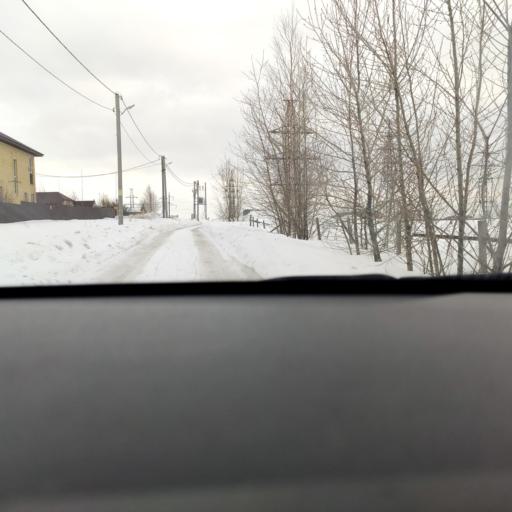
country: RU
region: Tatarstan
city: Vysokaya Gora
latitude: 55.8075
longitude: 49.2786
